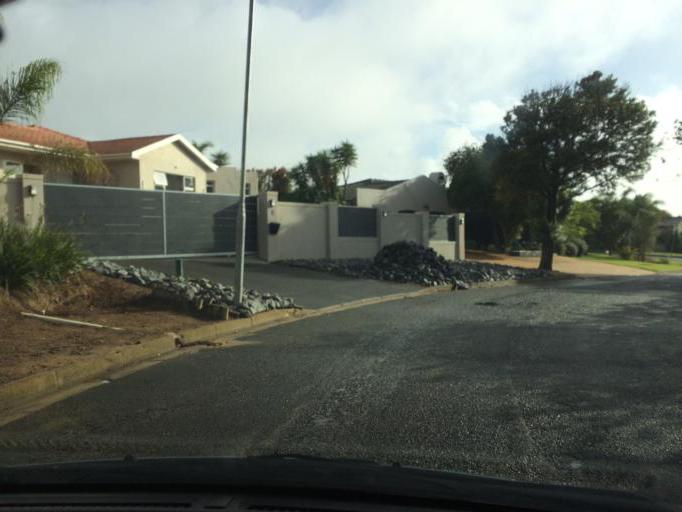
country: ZA
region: Western Cape
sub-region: City of Cape Town
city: Kraaifontein
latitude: -33.8667
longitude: 18.6481
